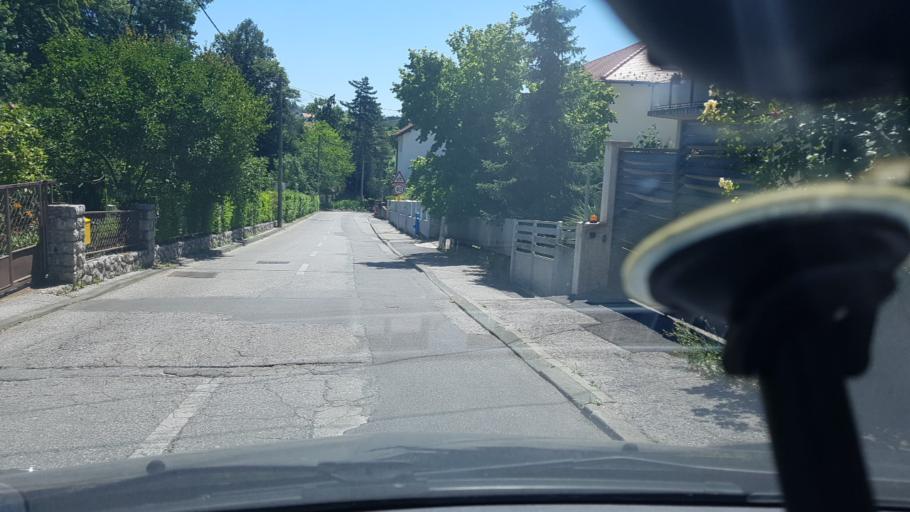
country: HR
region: Grad Zagreb
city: Zagreb
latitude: 45.8388
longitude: 15.9743
